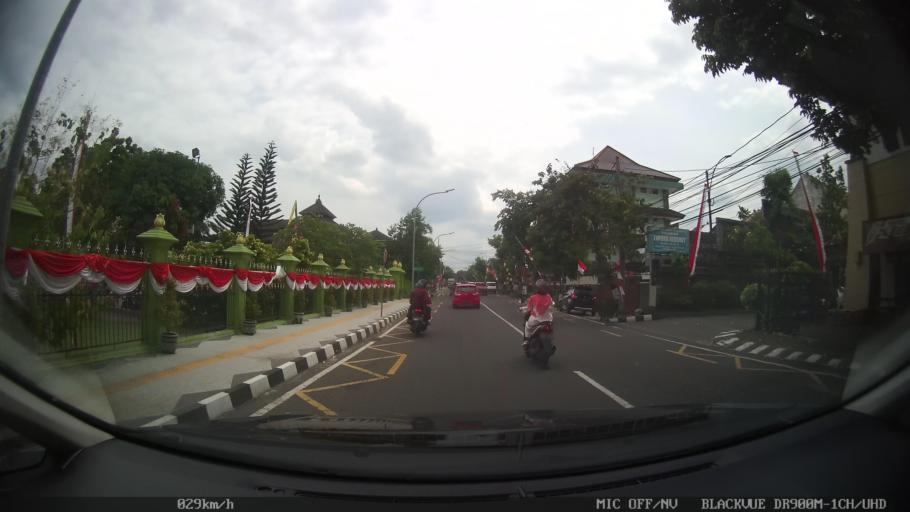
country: ID
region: Daerah Istimewa Yogyakarta
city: Yogyakarta
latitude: -7.7994
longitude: 110.3913
